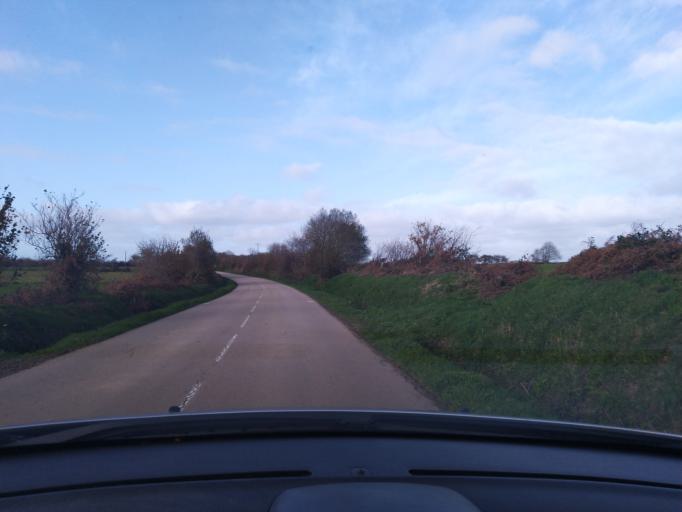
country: FR
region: Brittany
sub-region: Departement du Finistere
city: Plouigneau
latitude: 48.5365
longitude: -3.6732
